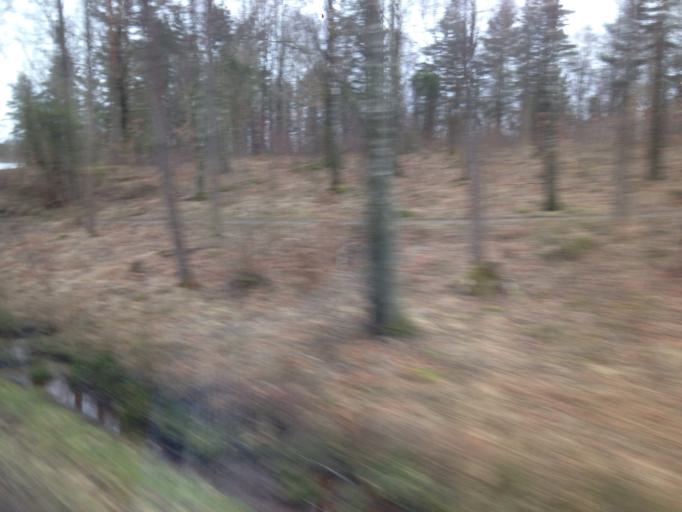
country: SE
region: Vaestra Goetaland
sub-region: Partille Kommun
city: Furulund
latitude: 57.7154
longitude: 12.1394
